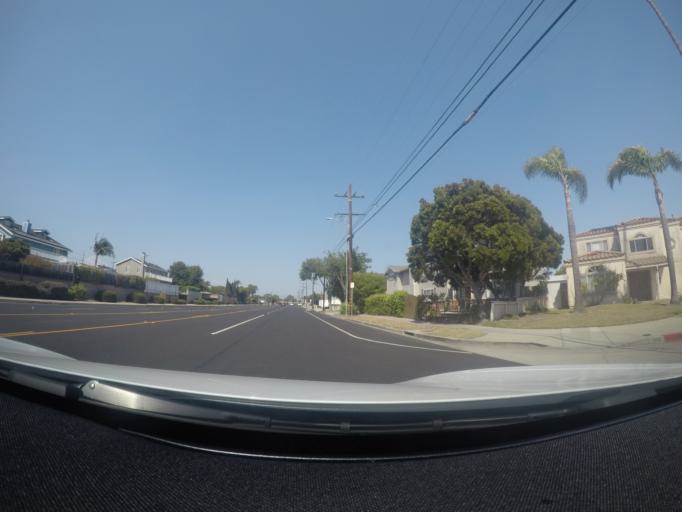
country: US
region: California
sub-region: Los Angeles County
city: Rolling Hills Estates
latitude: 33.8156
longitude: -118.3647
